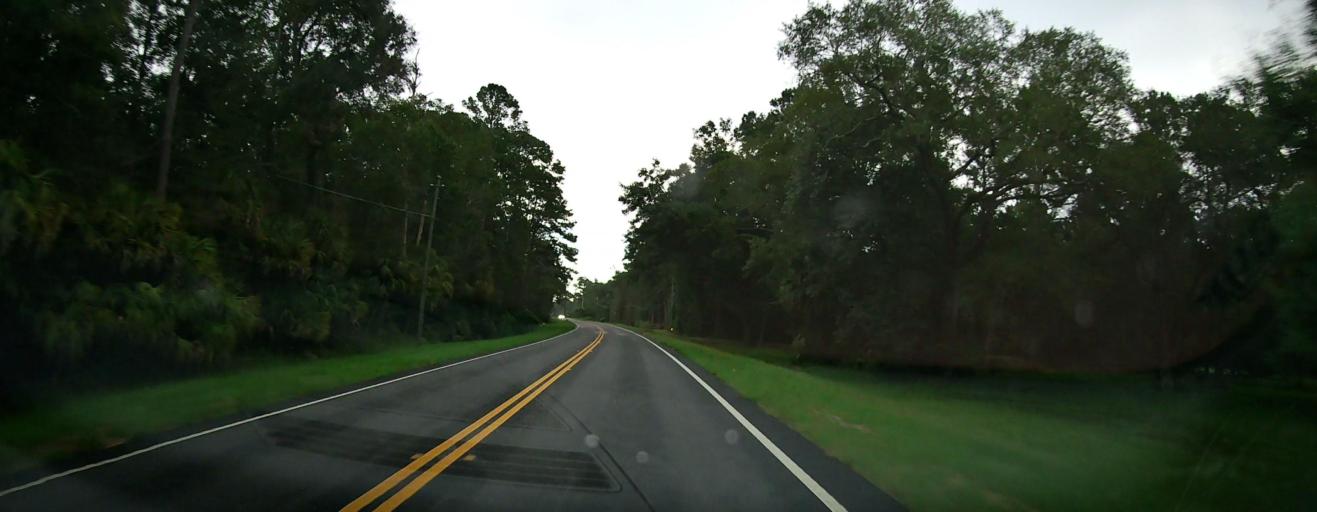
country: US
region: Georgia
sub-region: Glynn County
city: Dock Junction
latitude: 31.2936
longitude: -81.6953
